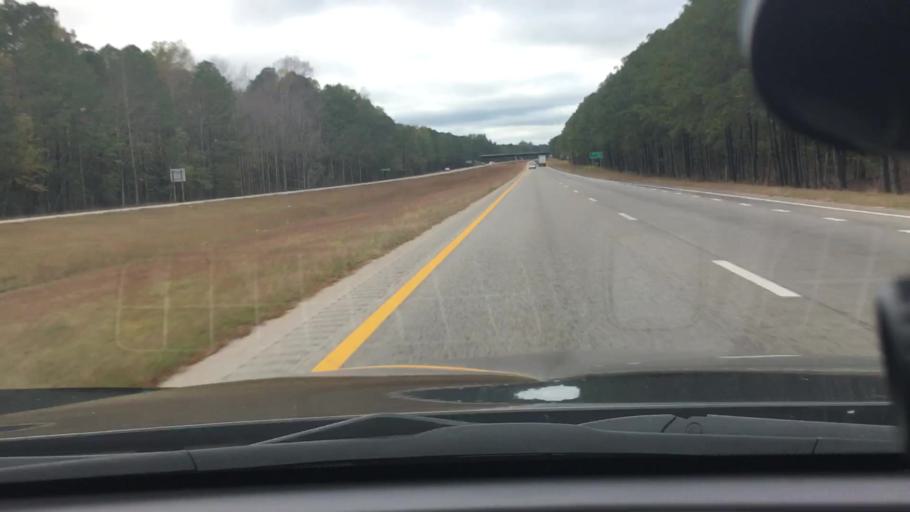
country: US
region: North Carolina
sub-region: Wilson County
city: Lucama
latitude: 35.7759
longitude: -78.0645
